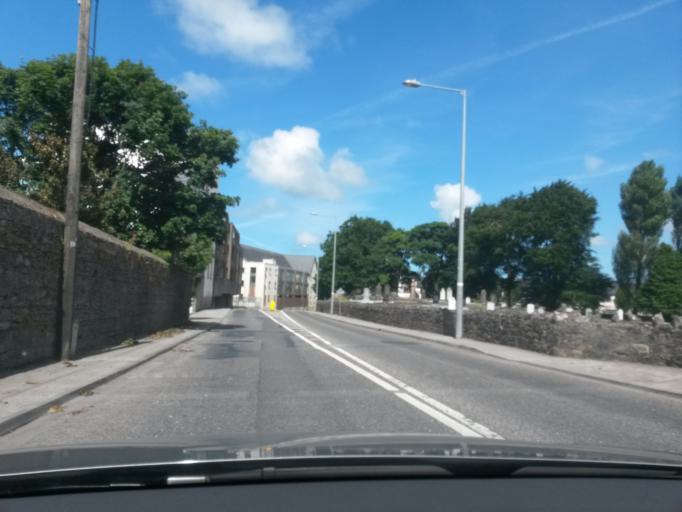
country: IE
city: Ballisodare
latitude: 54.2114
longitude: -8.5082
